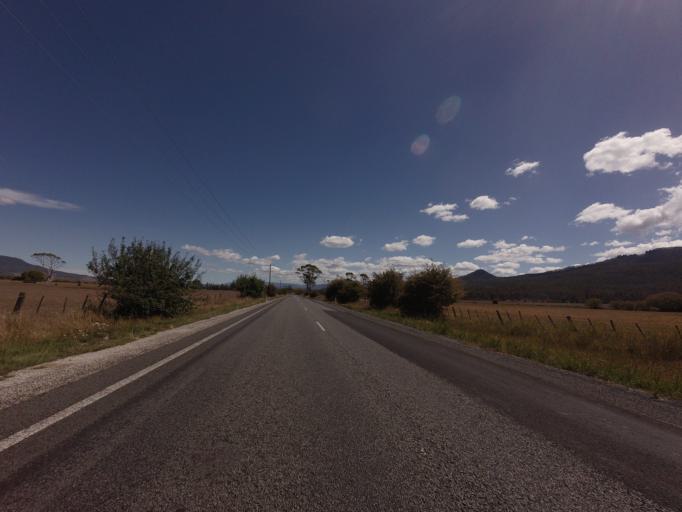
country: AU
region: Tasmania
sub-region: Break O'Day
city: St Helens
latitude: -41.5764
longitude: 148.1204
